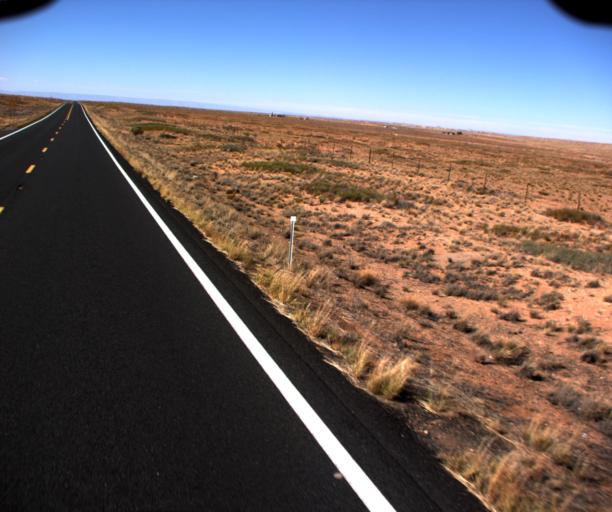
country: US
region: Arizona
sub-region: Coconino County
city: Tuba City
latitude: 36.0168
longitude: -111.1011
